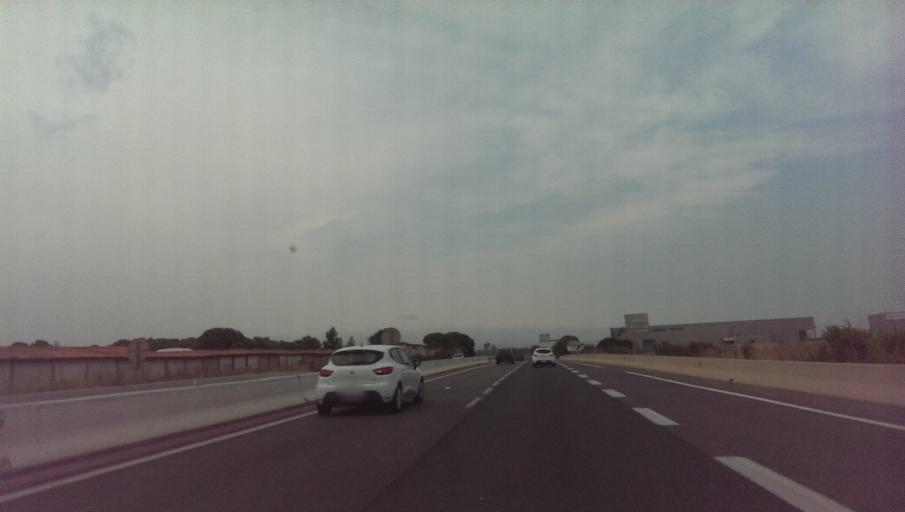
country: FR
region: Languedoc-Roussillon
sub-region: Departement des Pyrenees-Orientales
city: Pia
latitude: 42.7510
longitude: 2.8951
